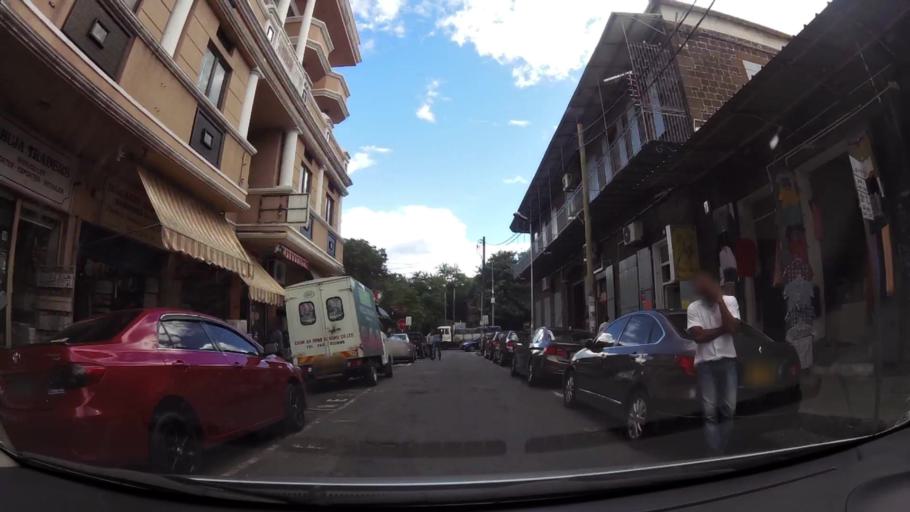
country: MU
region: Port Louis
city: Port Louis
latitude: -20.1600
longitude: 57.5028
